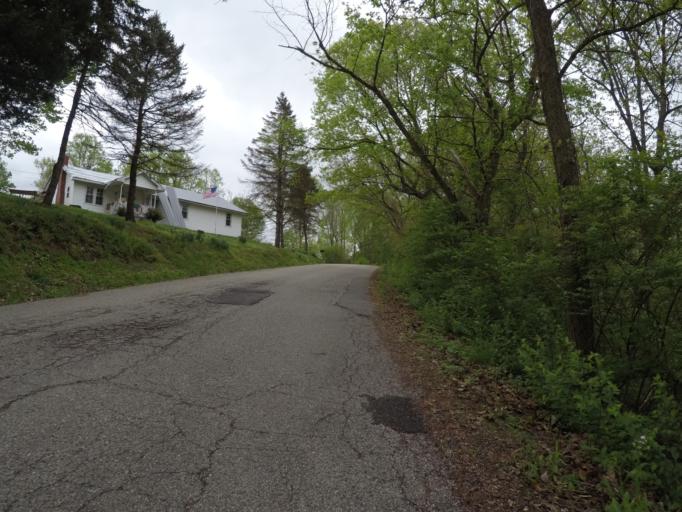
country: US
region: West Virginia
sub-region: Cabell County
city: Barboursville
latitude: 38.4000
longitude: -82.2635
